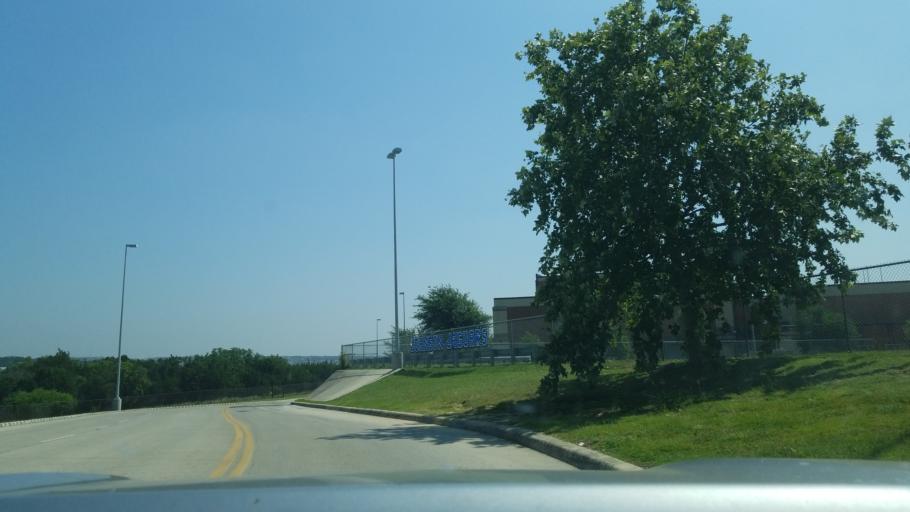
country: US
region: Texas
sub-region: Bexar County
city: Timberwood Park
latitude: 29.6579
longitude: -98.4372
